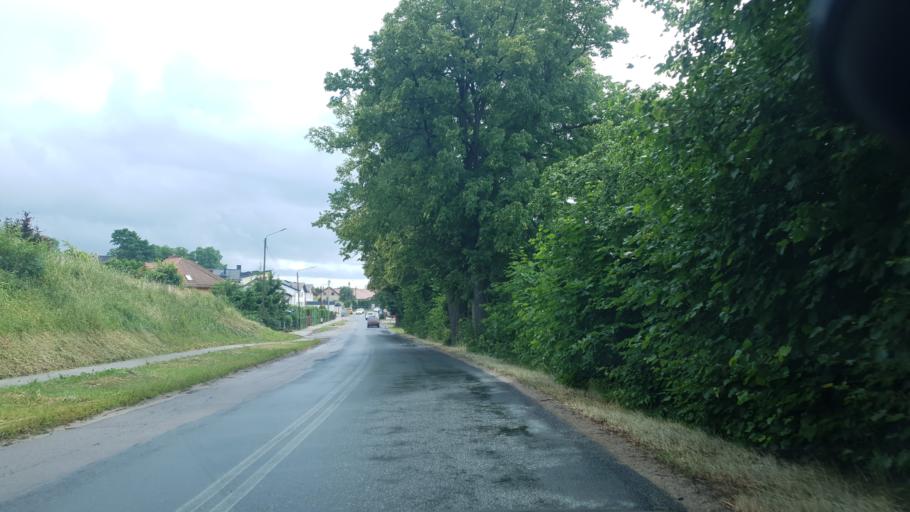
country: PL
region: Pomeranian Voivodeship
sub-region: Powiat kartuski
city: Chmielno
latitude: 54.2719
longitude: 18.0847
